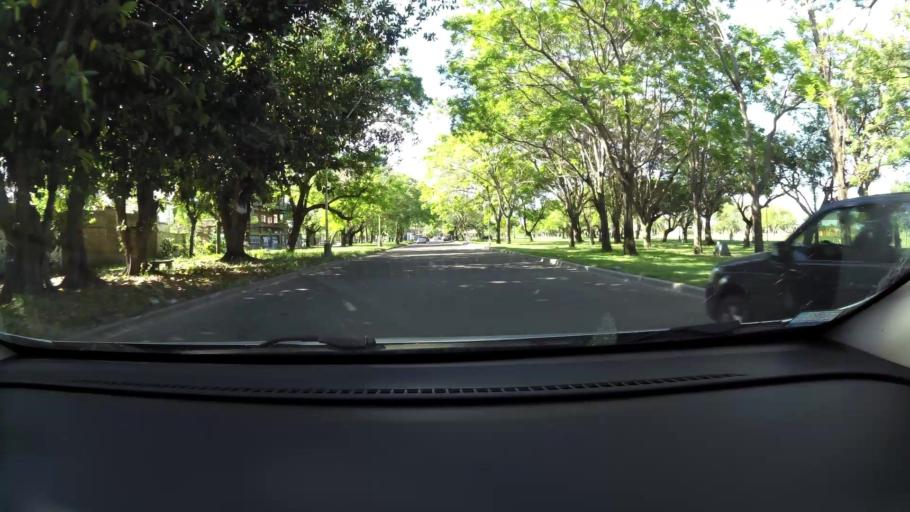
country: AR
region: Santa Fe
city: Santa Fe de la Vera Cruz
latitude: -31.6245
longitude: -60.6976
